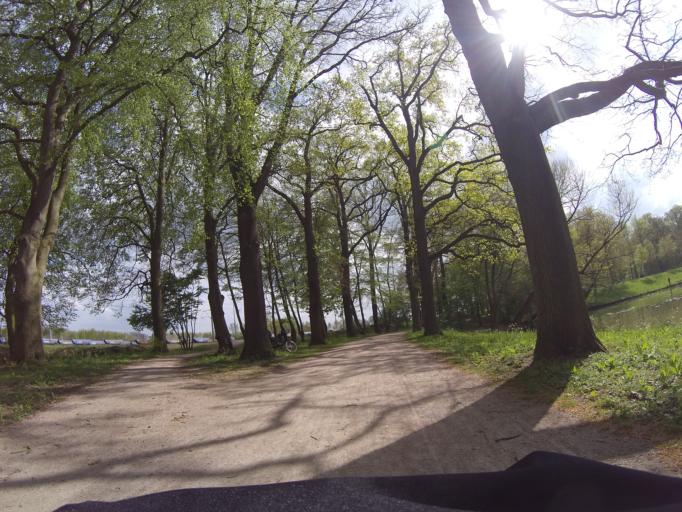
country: NL
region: Gelderland
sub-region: Gemeente Hattem
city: Hattem
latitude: 52.4949
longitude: 6.0723
